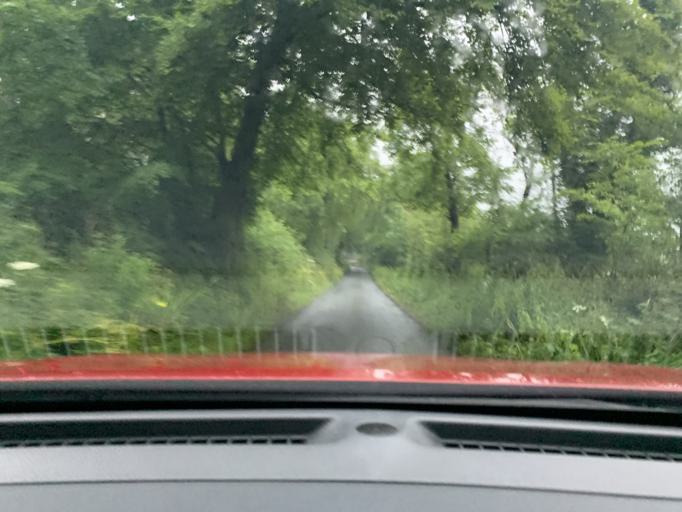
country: IE
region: Connaught
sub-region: Sligo
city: Sligo
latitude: 54.3245
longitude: -8.4460
